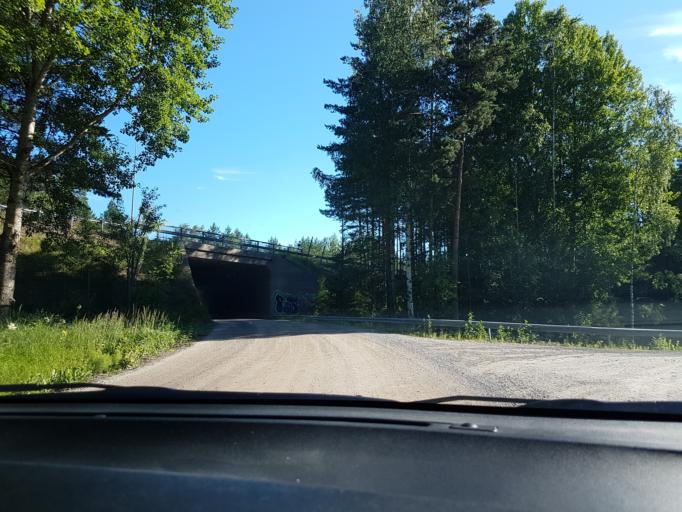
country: FI
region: Uusimaa
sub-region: Helsinki
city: Sibbo
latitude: 60.2717
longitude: 25.2330
